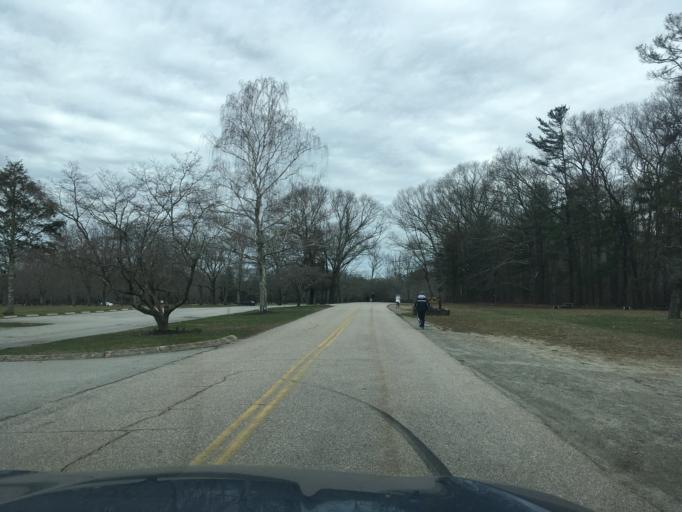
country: US
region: Rhode Island
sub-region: Kent County
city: East Greenwich
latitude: 41.6576
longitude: -71.4405
